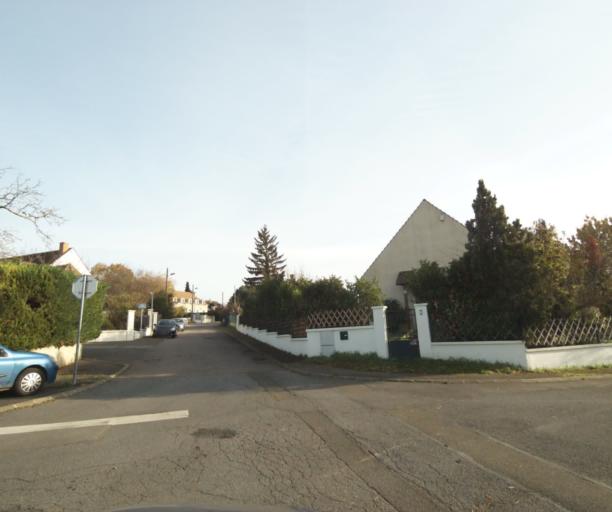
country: FR
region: Ile-de-France
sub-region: Departement des Yvelines
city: Triel-sur-Seine
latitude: 48.9722
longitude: 2.0010
